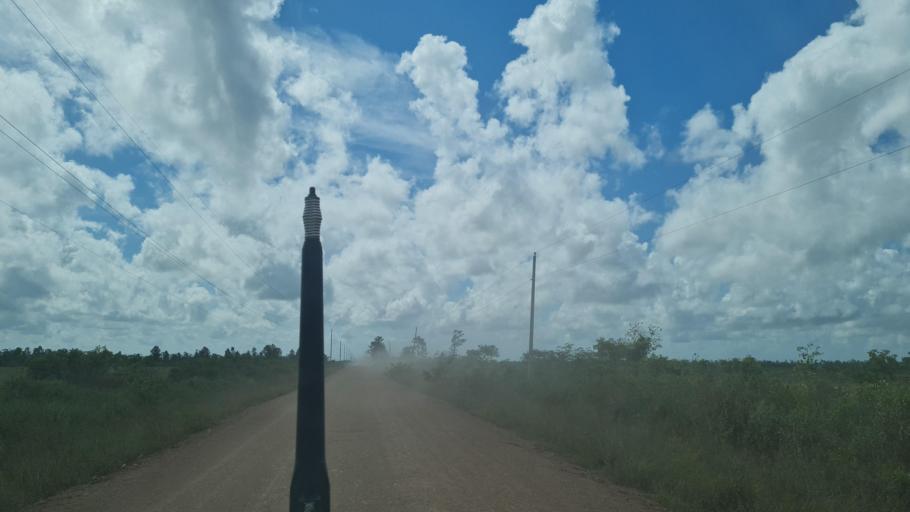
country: NI
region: Atlantico Norte (RAAN)
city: Puerto Cabezas
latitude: 14.1109
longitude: -83.6264
